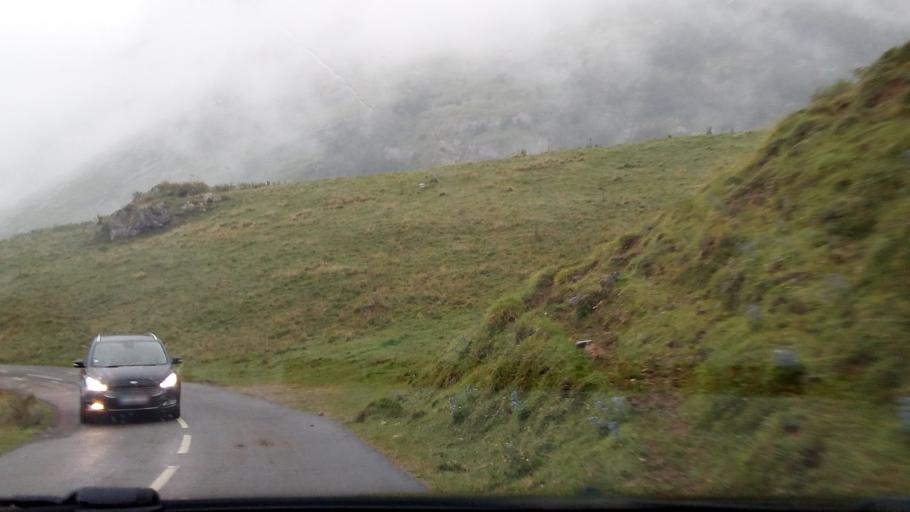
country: FR
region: Aquitaine
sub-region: Departement des Pyrenees-Atlantiques
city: Laruns
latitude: 42.9667
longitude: -0.3028
